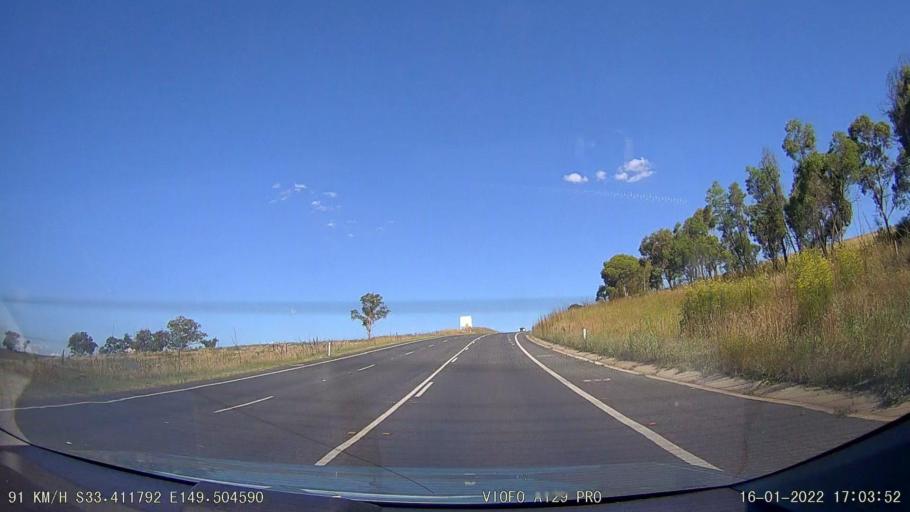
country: AU
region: New South Wales
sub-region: Bathurst Regional
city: Eglinton
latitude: -33.4117
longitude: 149.5044
